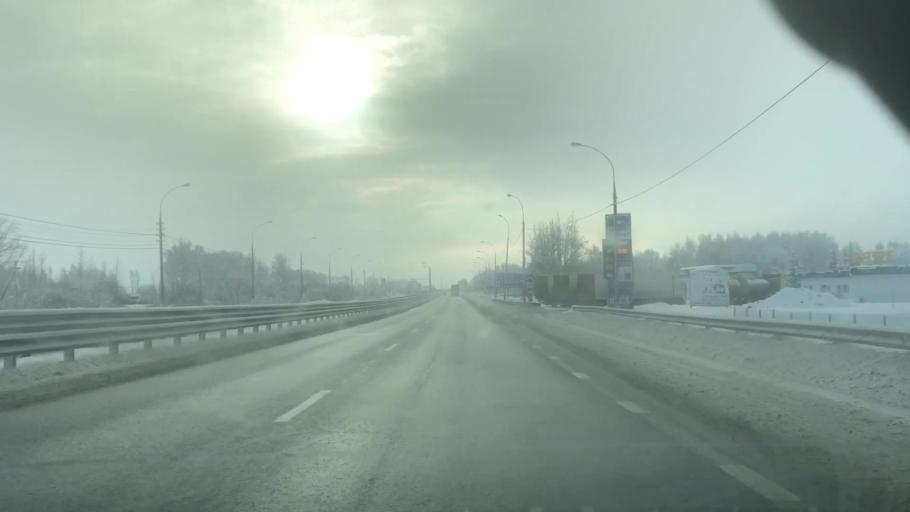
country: RU
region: Tula
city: Venev
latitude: 54.3429
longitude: 38.1545
